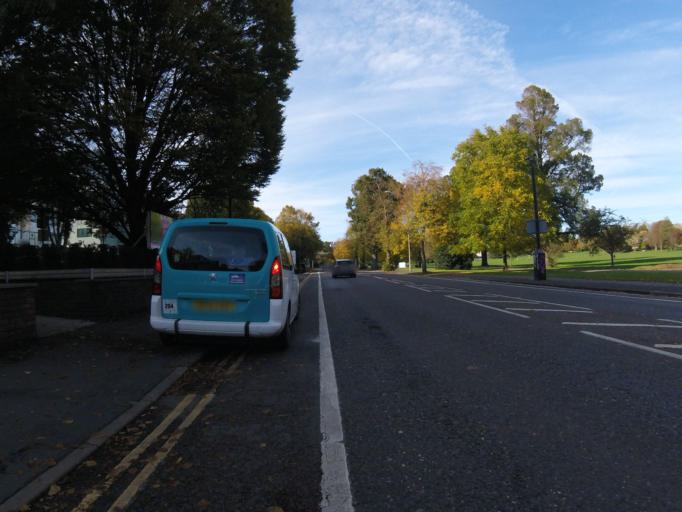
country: GB
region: England
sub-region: Brighton and Hove
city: Brighton
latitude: 50.8383
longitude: -0.1469
